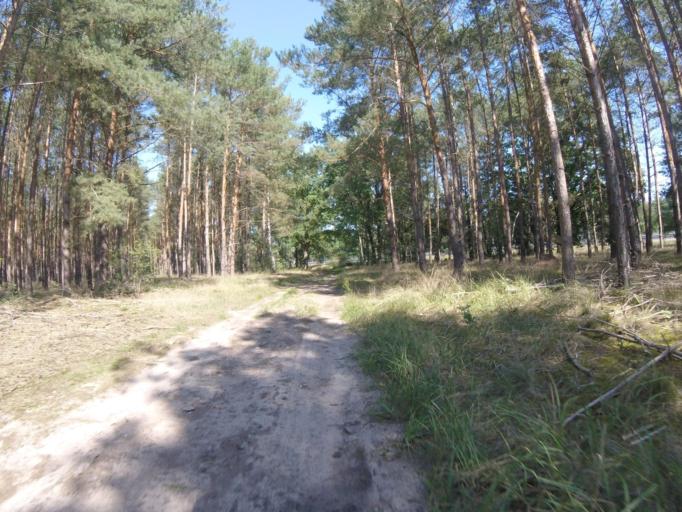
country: DE
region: Brandenburg
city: Bestensee
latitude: 52.2261
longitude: 13.5941
